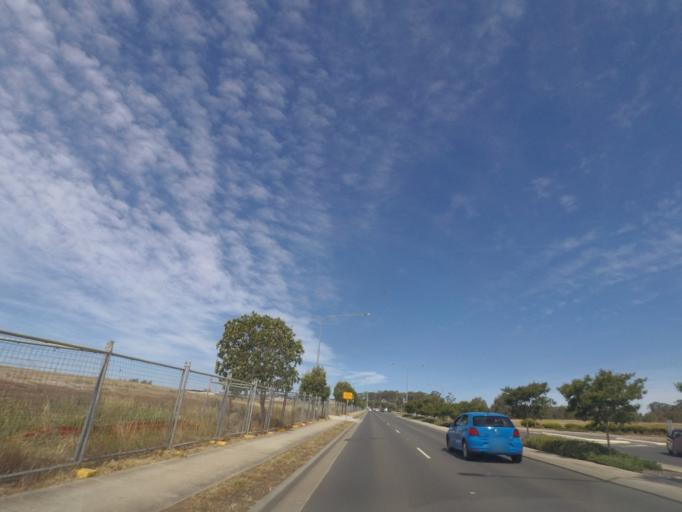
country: AU
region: New South Wales
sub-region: Camden
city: Narellan Vale
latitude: -34.0233
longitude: 150.7685
